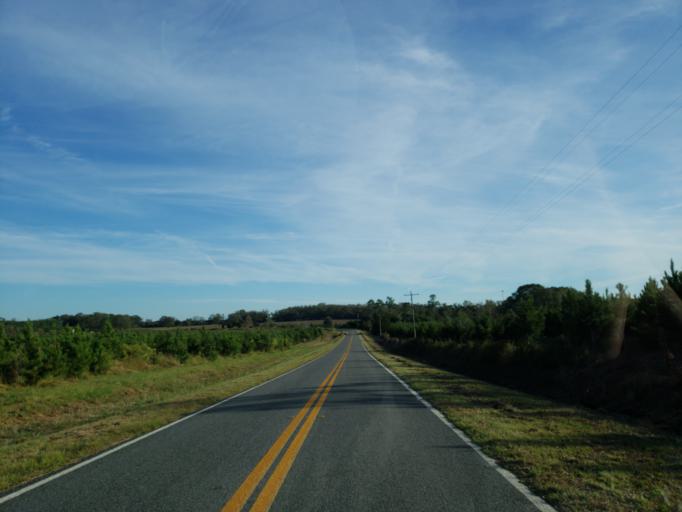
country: US
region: Georgia
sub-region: Dooly County
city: Vienna
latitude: 32.0367
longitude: -83.7528
